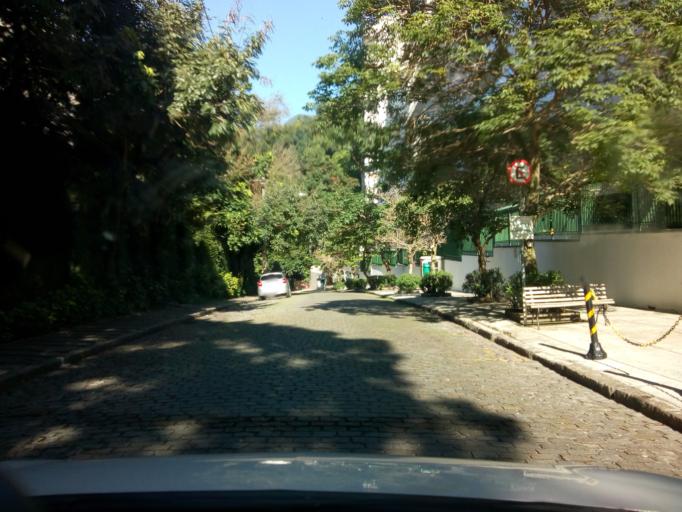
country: BR
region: Rio de Janeiro
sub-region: Rio De Janeiro
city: Rio de Janeiro
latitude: -22.9854
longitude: -43.2340
